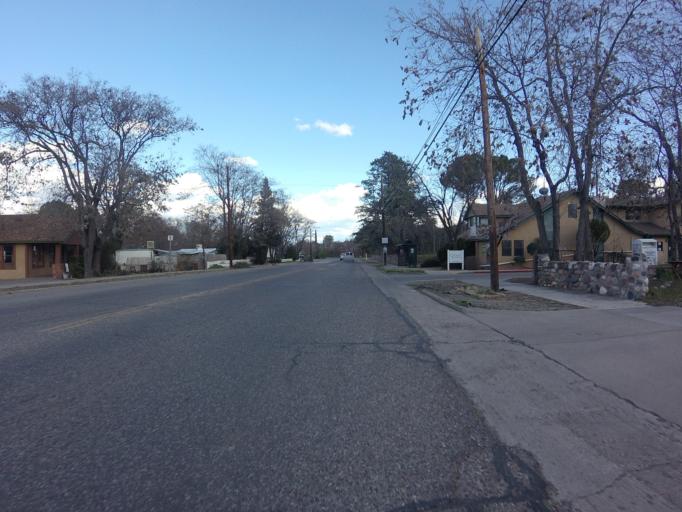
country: US
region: Arizona
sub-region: Yavapai County
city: Cottonwood
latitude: 34.7445
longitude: -112.0233
